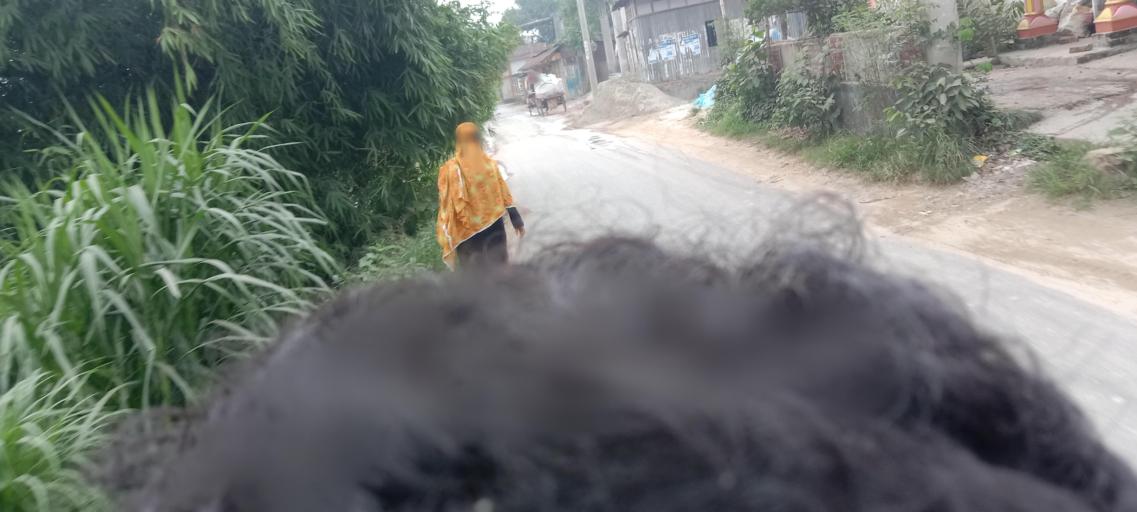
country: BD
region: Dhaka
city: Azimpur
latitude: 23.7409
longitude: 90.3128
